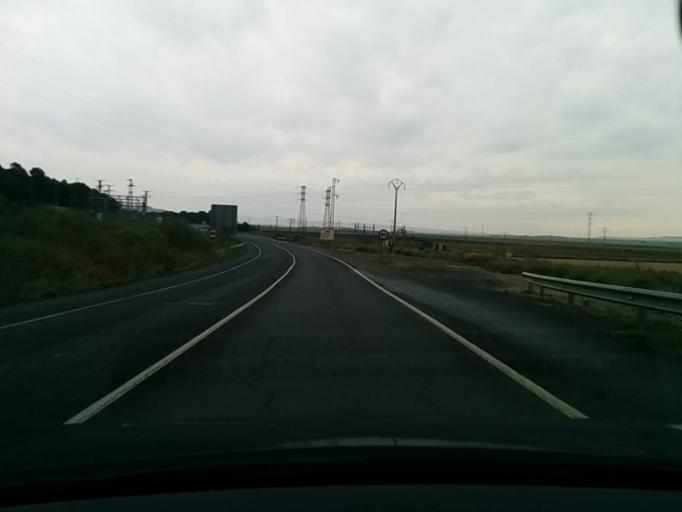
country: ES
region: Navarre
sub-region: Provincia de Navarra
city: Cadreita
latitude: 42.2087
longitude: -1.6637
